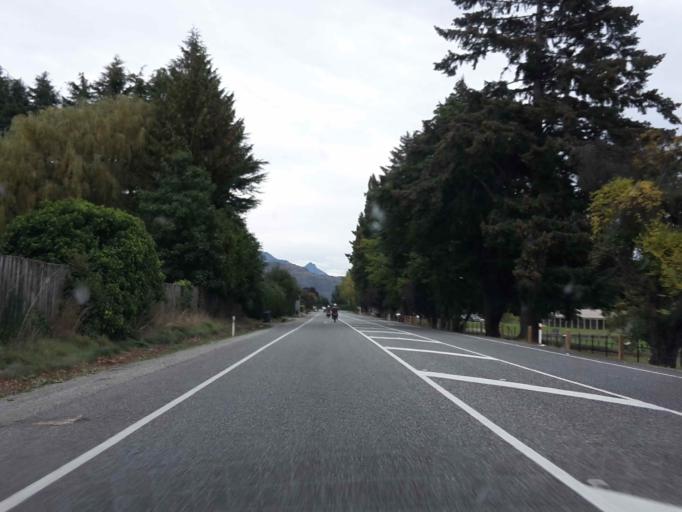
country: NZ
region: Otago
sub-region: Queenstown-Lakes District
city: Arrowtown
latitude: -44.9893
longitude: 168.8120
